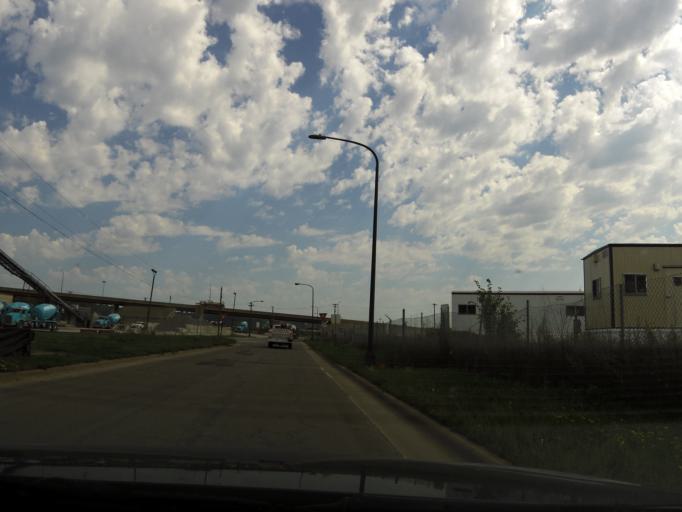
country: US
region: Minnesota
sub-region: Ramsey County
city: Saint Paul
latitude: 44.9430
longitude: -93.0544
